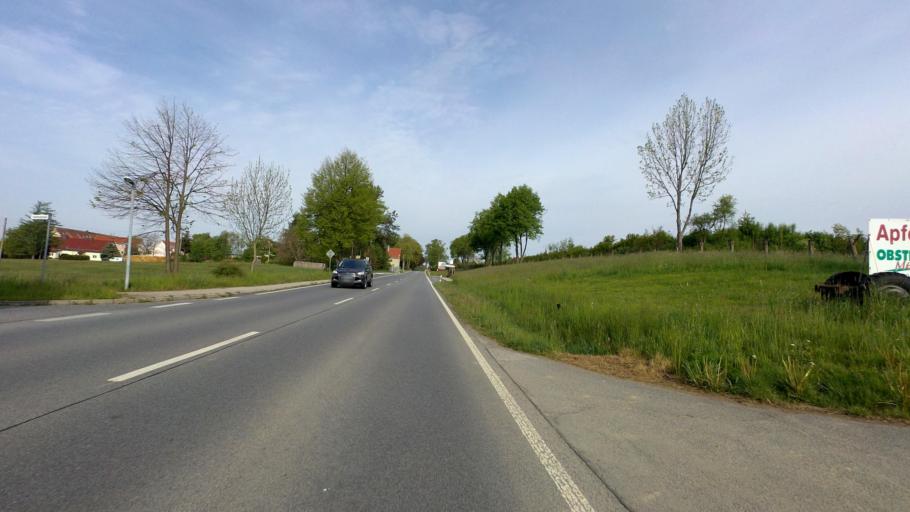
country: DE
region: Saxony
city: Stolpen
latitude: 51.0447
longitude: 14.1022
